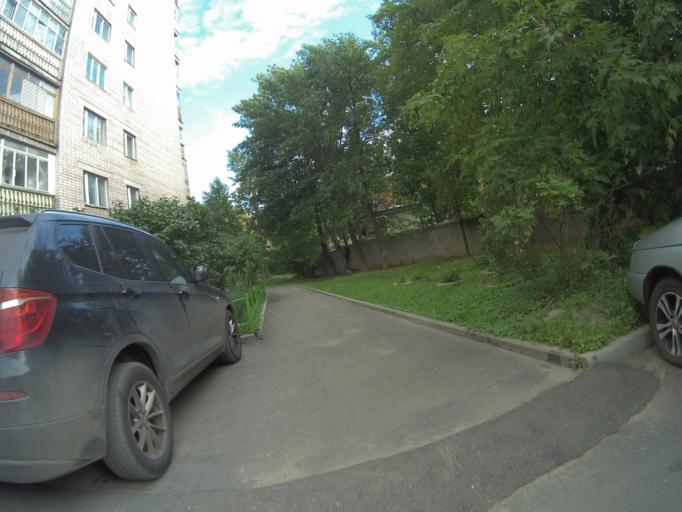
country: RU
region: Vladimir
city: Vladimir
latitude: 56.1513
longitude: 40.4274
